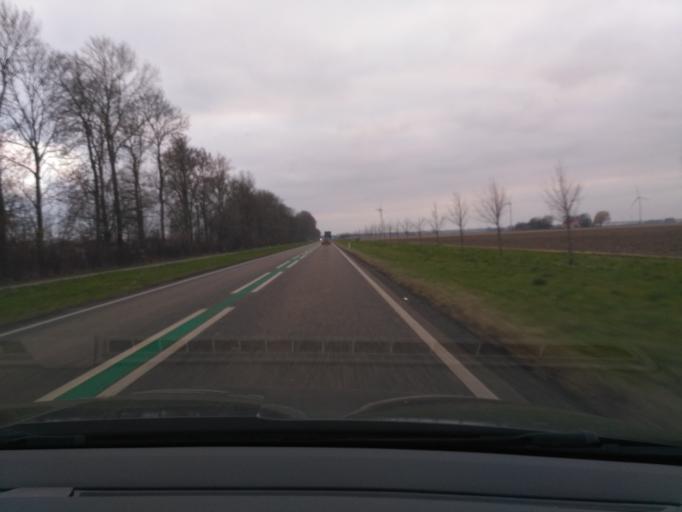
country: NL
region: Flevoland
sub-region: Gemeente Dronten
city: Dronten
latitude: 52.4889
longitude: 5.7147
